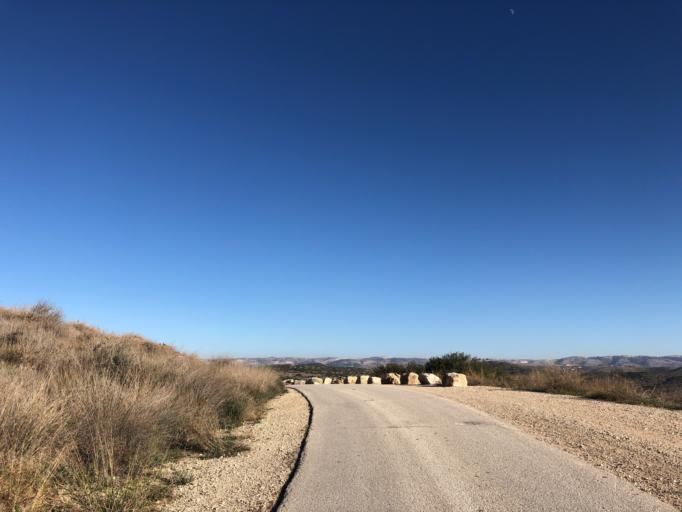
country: PS
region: West Bank
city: Idhna
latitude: 31.5919
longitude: 34.8976
